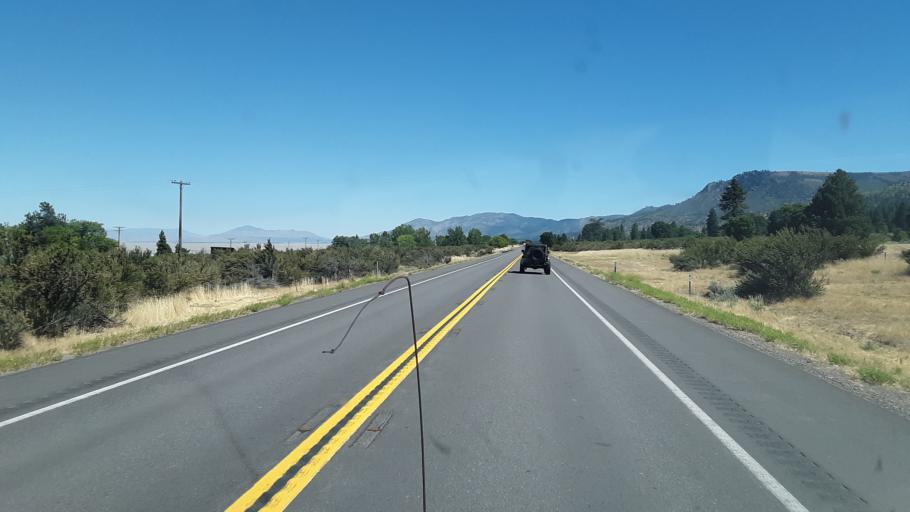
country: US
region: California
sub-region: Lassen County
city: Janesville
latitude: 40.2702
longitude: -120.4784
